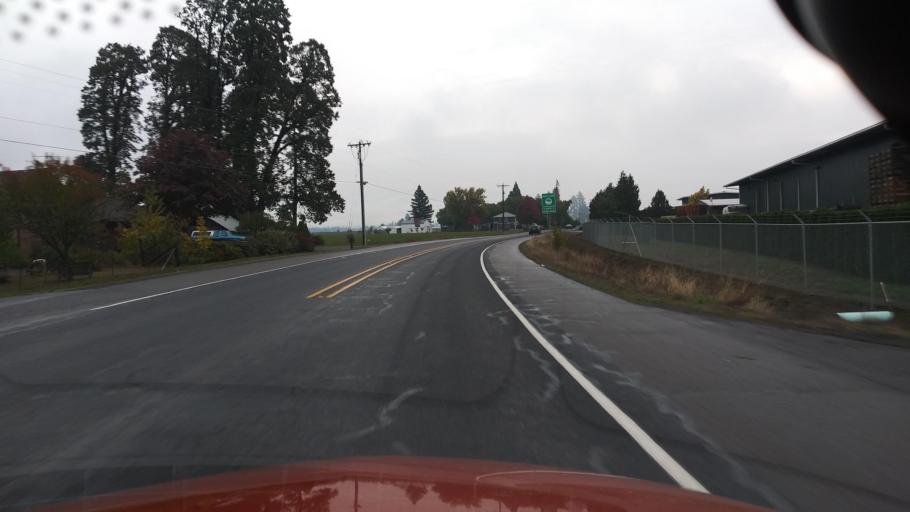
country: US
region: Oregon
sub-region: Washington County
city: Cornelius
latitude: 45.5709
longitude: -123.0455
